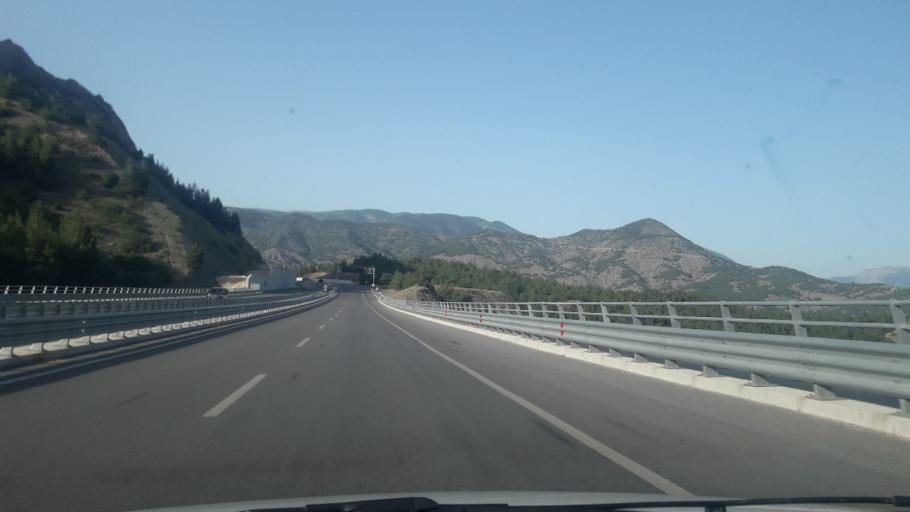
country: TR
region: Amasya
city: Amasya
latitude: 40.6791
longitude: 35.8086
